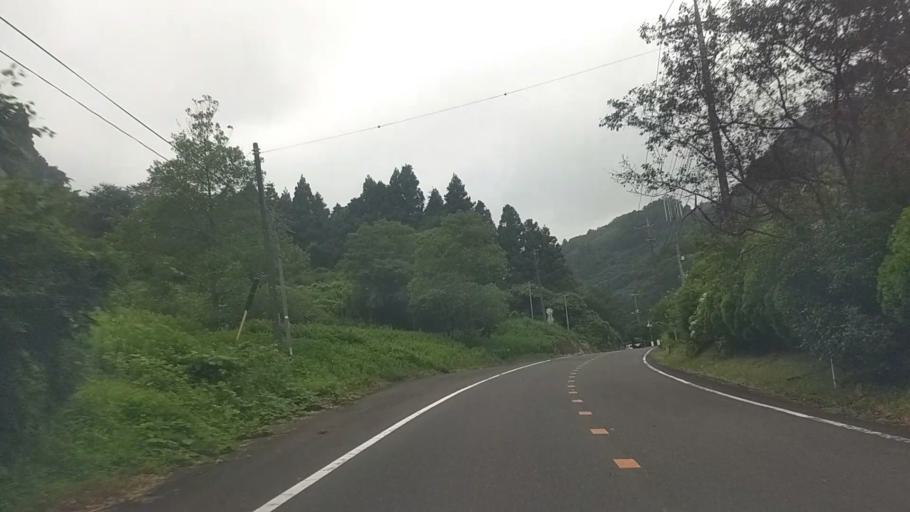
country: JP
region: Chiba
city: Kawaguchi
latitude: 35.1416
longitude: 139.9457
